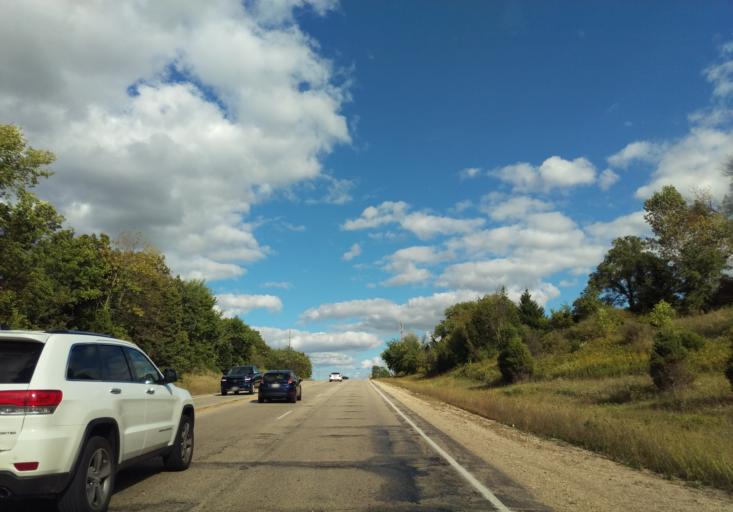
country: US
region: Wisconsin
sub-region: Rock County
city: Janesville
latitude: 42.7301
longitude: -89.0518
